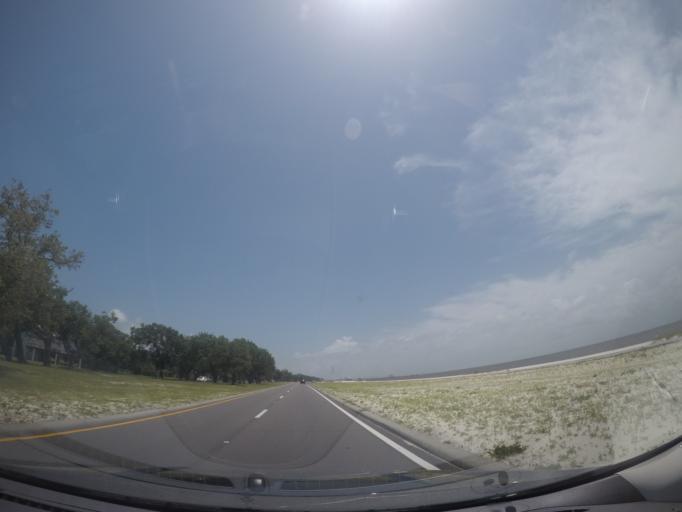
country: US
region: Mississippi
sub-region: Harrison County
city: Long Beach
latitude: 30.3413
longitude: -89.1600
